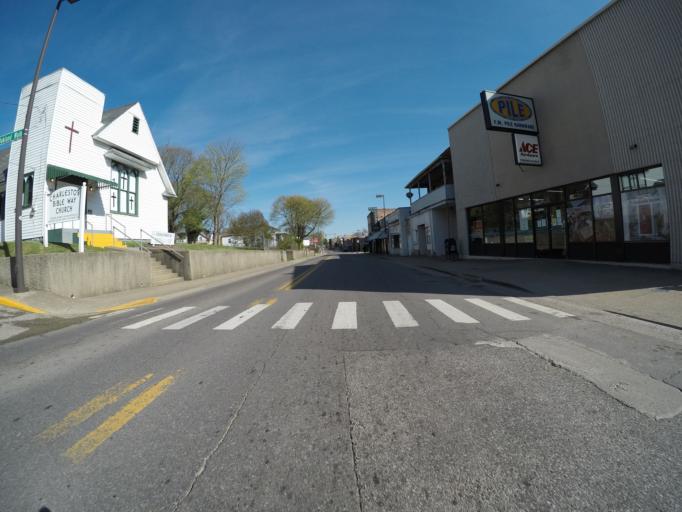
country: US
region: West Virginia
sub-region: Kanawha County
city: Charleston
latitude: 38.3725
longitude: -81.6619
